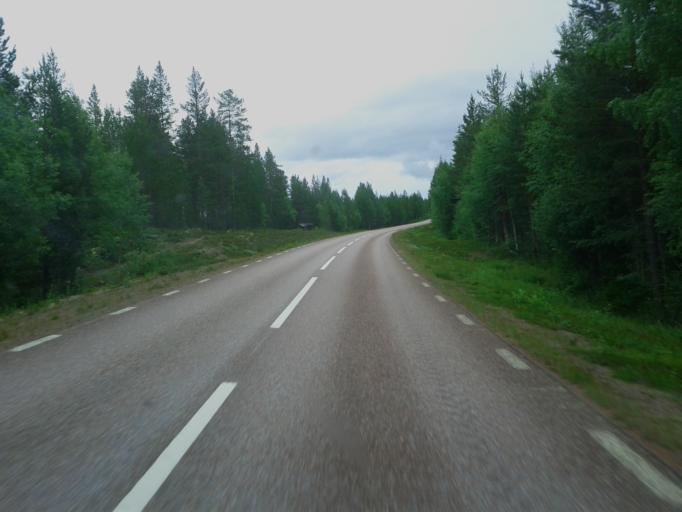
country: NO
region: Hedmark
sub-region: Trysil
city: Innbygda
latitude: 61.7157
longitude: 13.0055
